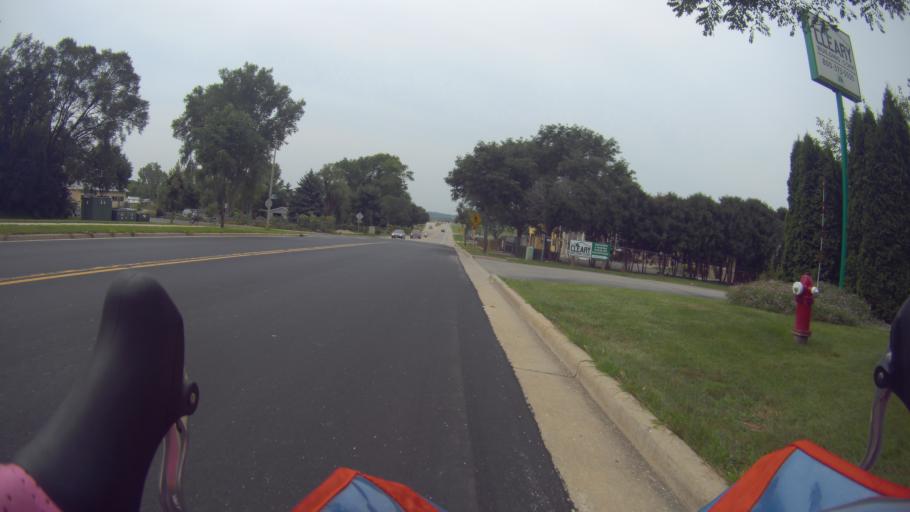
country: US
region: Wisconsin
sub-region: Dane County
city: Verona
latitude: 42.9795
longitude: -89.5415
